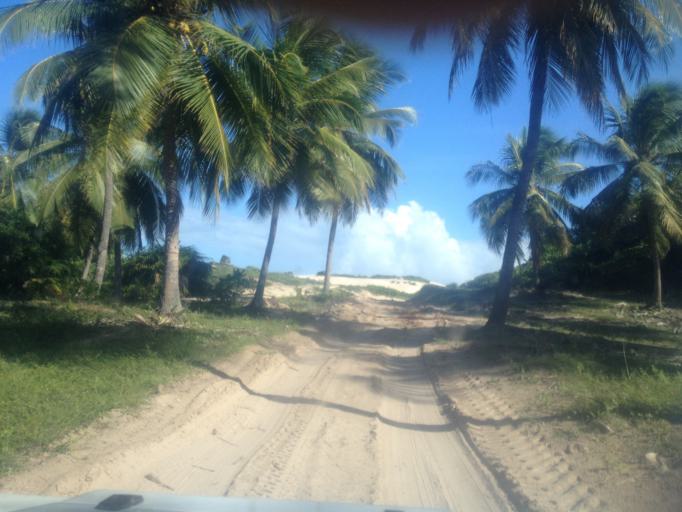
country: BR
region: Sergipe
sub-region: Indiaroba
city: Indiaroba
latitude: -11.4679
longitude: -37.3709
